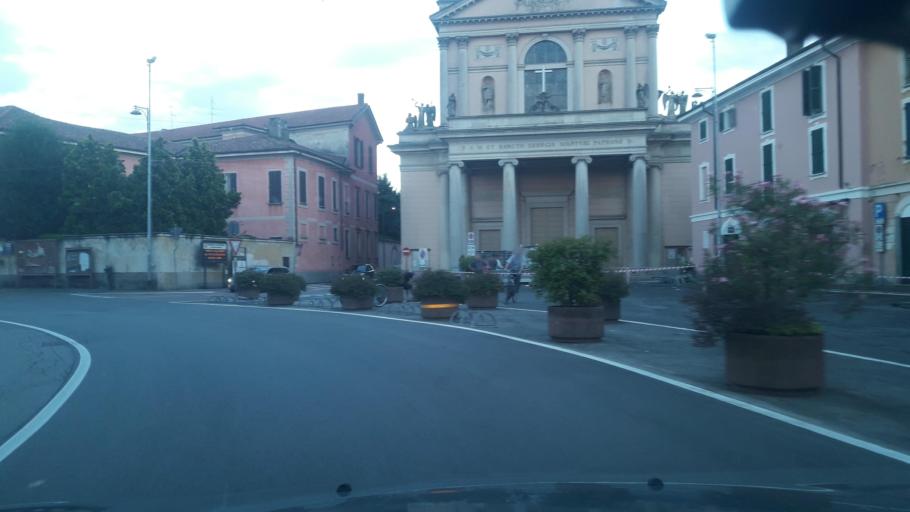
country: IT
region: Lombardy
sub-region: Citta metropolitana di Milano
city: Cuggiono
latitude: 45.5065
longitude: 8.8150
